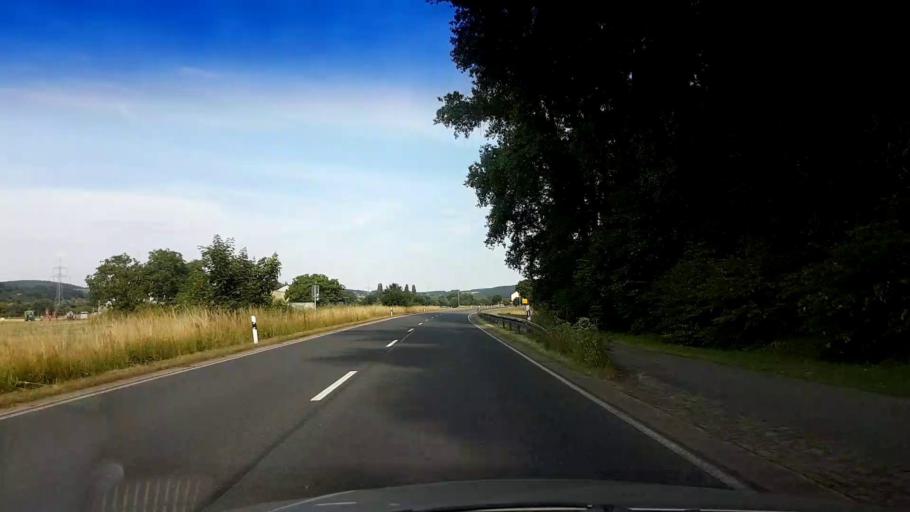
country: DE
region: Bavaria
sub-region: Regierungsbezirk Unterfranken
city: Eltmann
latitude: 49.9689
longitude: 10.6881
